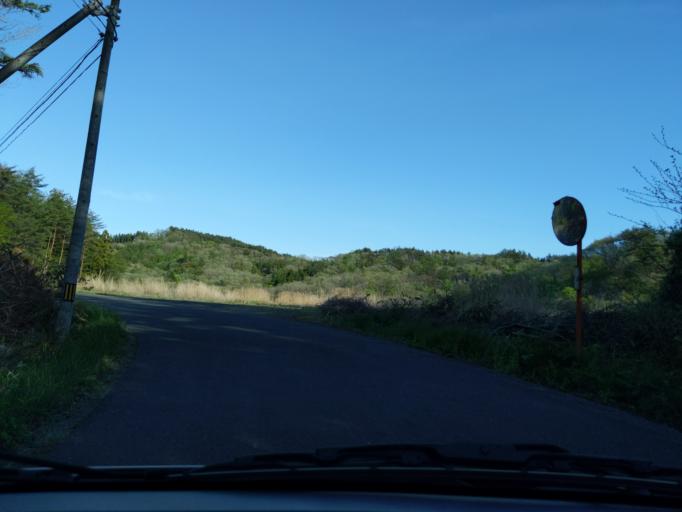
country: JP
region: Iwate
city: Ichinoseki
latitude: 38.8740
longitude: 140.9212
